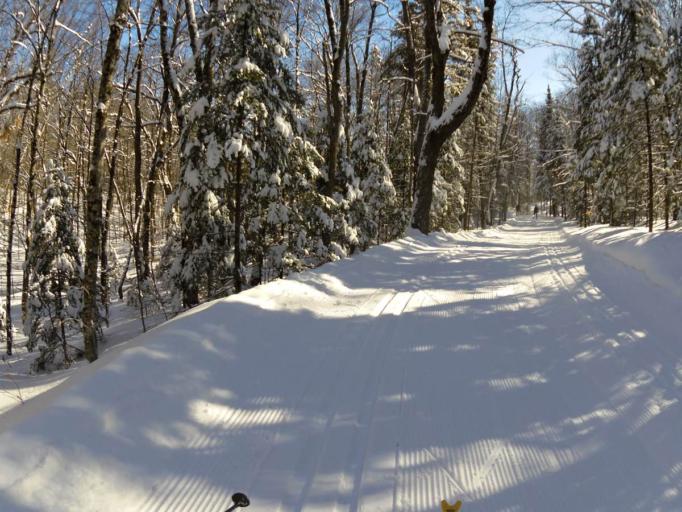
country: CA
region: Quebec
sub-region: Outaouais
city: Wakefield
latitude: 45.5679
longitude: -75.9243
